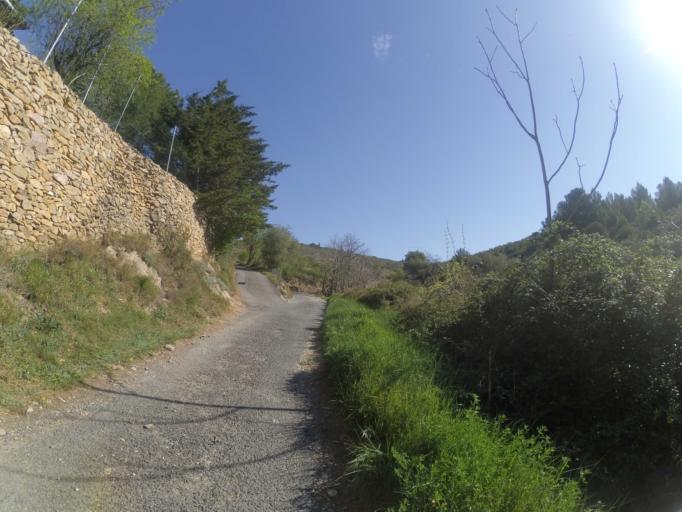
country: FR
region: Languedoc-Roussillon
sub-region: Departement des Pyrenees-Orientales
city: Estagel
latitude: 42.7614
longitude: 2.7532
